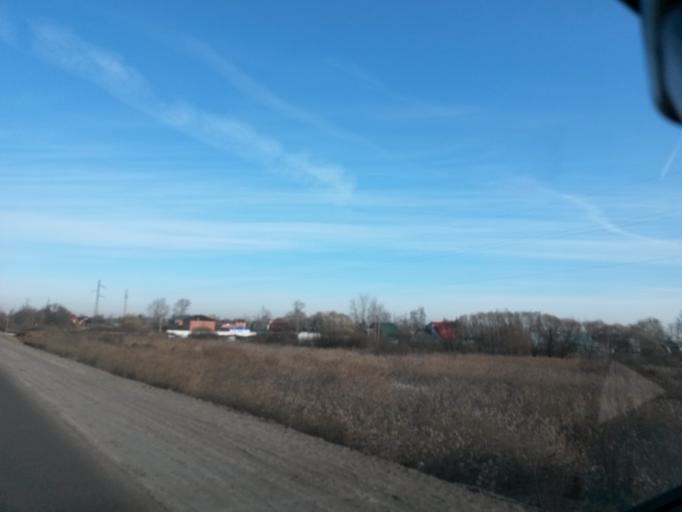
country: RU
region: Jaroslavl
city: Yaroslavl
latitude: 57.6000
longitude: 39.7990
